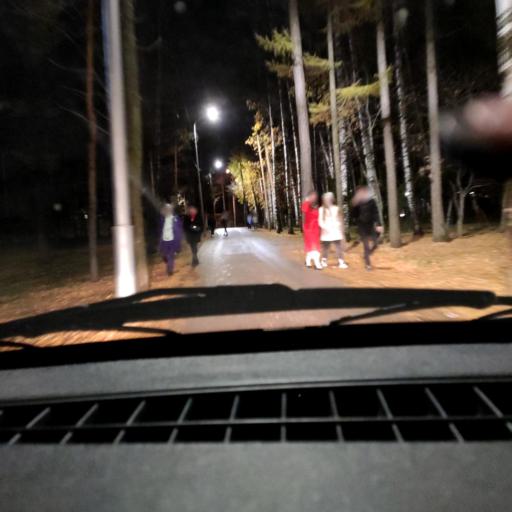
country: RU
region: Bashkortostan
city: Ufa
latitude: 54.8253
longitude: 56.0562
